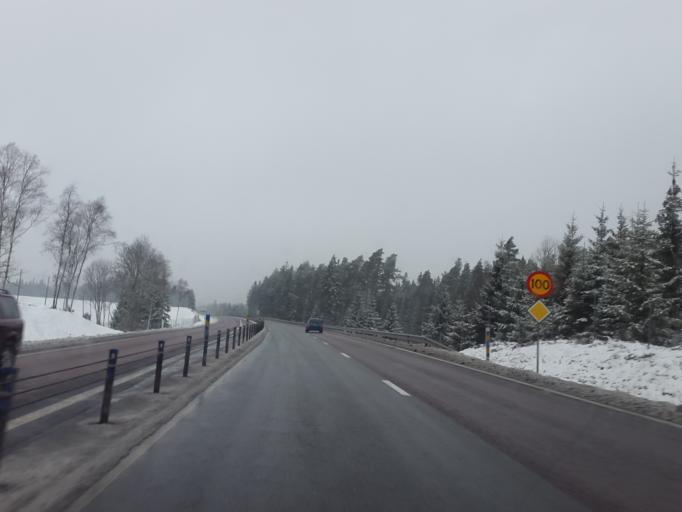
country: SE
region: Joenkoeping
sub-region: Jonkopings Kommun
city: Taberg
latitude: 57.7544
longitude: 13.9370
